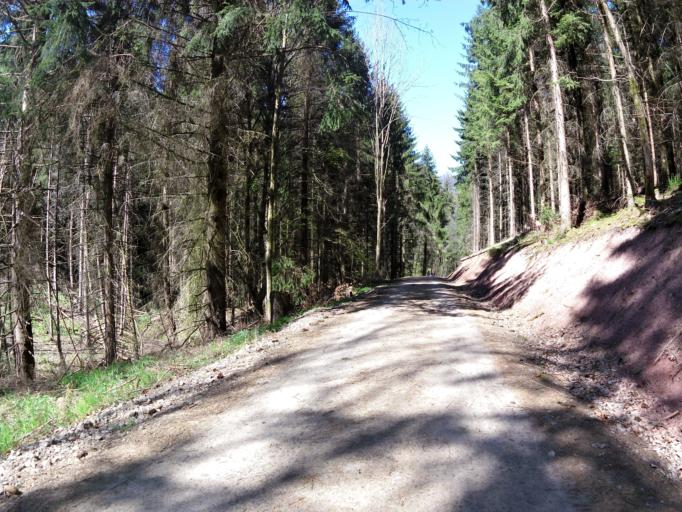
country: DE
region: Thuringia
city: Krauthausen
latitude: 50.9753
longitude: 10.2442
